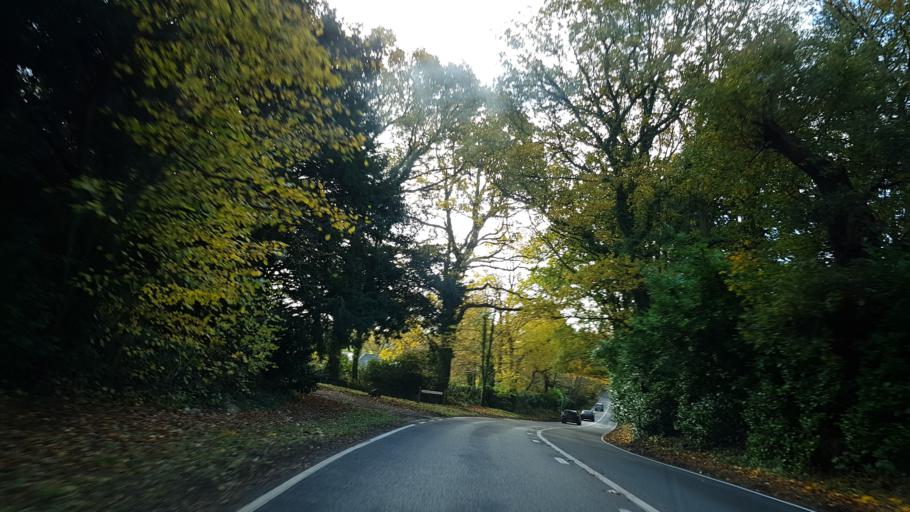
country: GB
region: England
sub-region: Surrey
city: Haslemere
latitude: 51.1242
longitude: -0.6735
